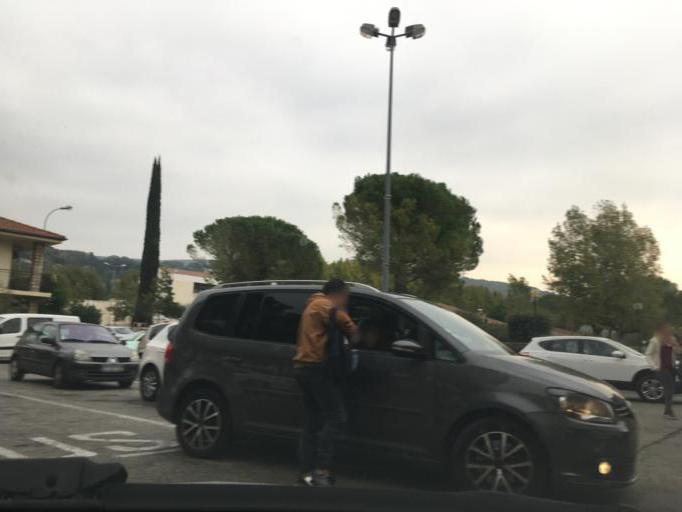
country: FR
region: Provence-Alpes-Cote d'Azur
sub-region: Departement du Var
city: Draguignan
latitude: 43.5352
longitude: 6.4717
